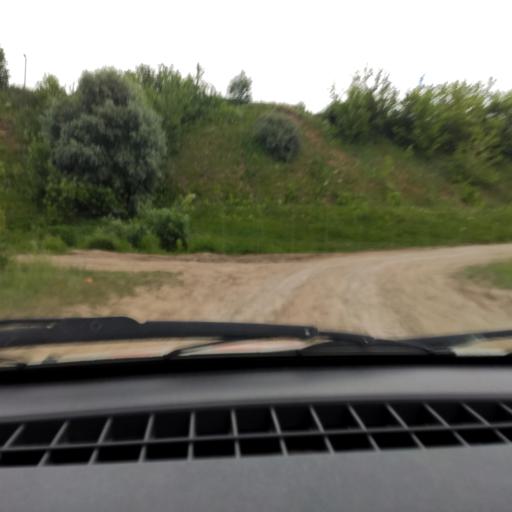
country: RU
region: Bashkortostan
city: Iglino
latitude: 54.7954
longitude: 56.2323
